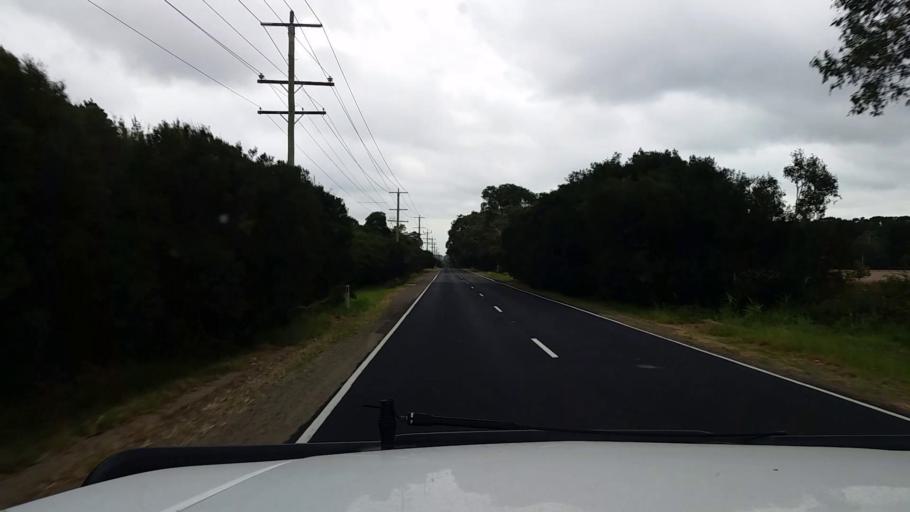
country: AU
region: Victoria
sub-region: Mornington Peninsula
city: Somerville
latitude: -38.2140
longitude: 145.1565
